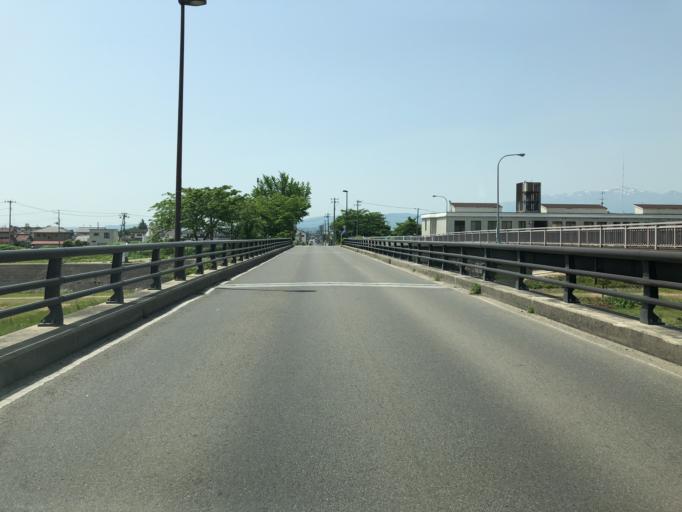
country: JP
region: Fukushima
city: Fukushima-shi
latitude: 37.7816
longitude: 140.4262
